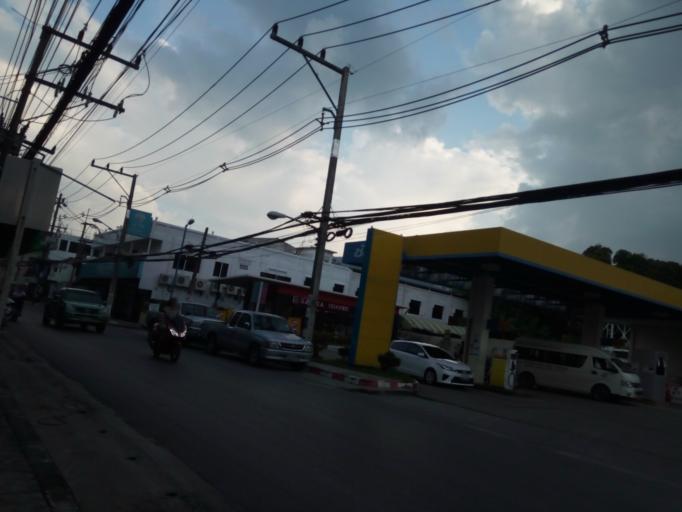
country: TH
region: Surat Thani
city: Ko Samui
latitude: 9.5353
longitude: 99.9358
